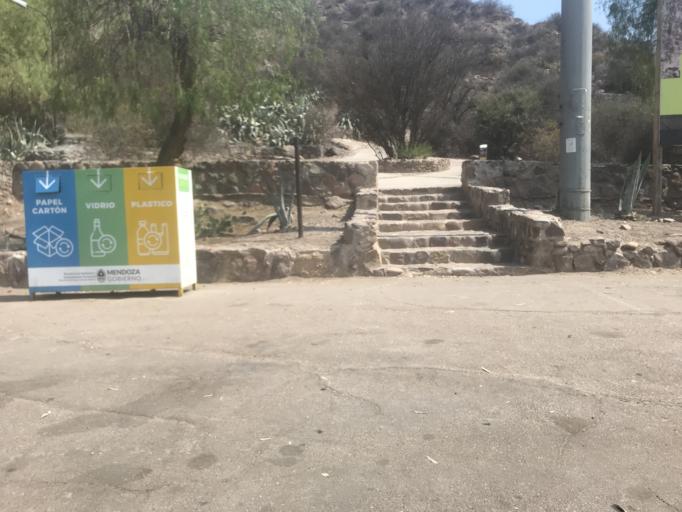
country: AR
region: Mendoza
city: Mendoza
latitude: -32.8846
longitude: -68.8893
